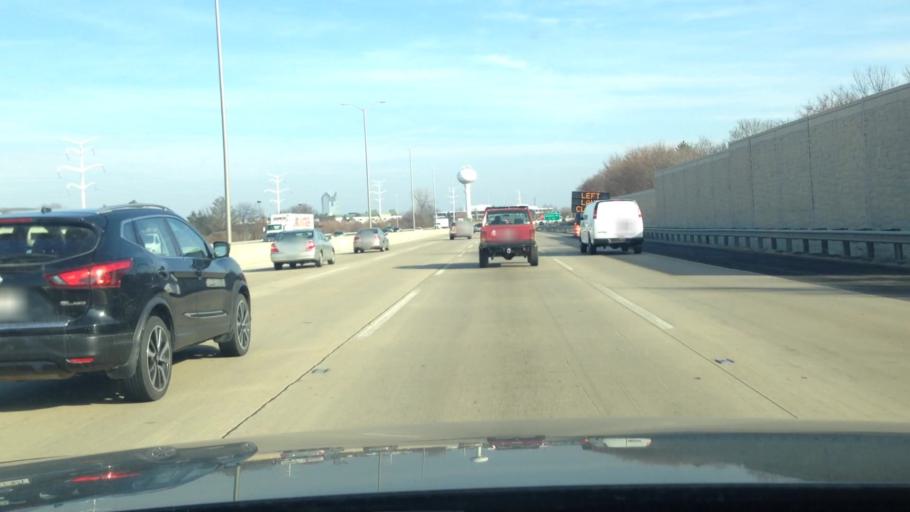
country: US
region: Illinois
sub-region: DuPage County
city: Oakbrook Terrace
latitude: 41.8416
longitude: -87.9848
